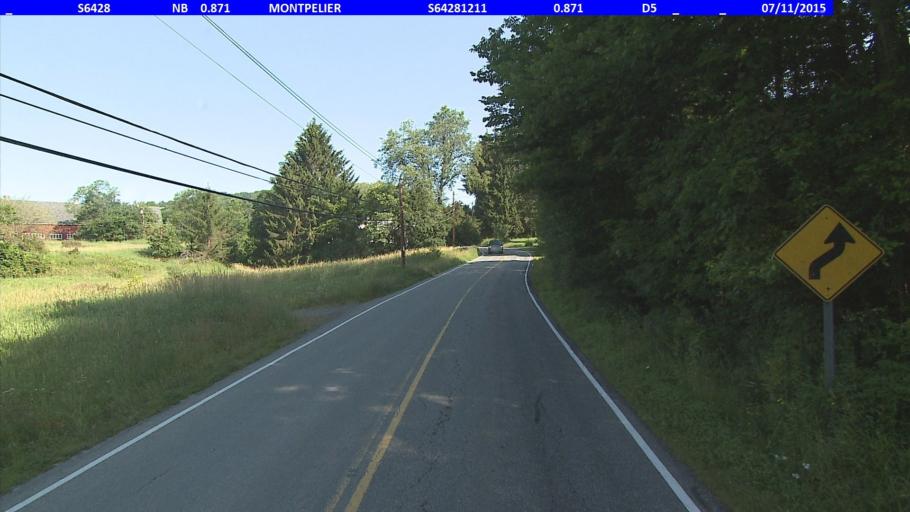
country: US
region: Vermont
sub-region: Washington County
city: Montpelier
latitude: 44.2742
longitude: -72.5925
